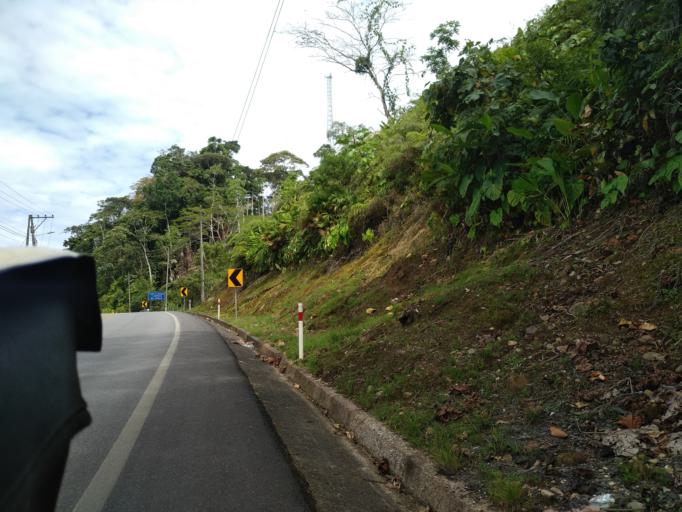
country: EC
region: Napo
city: Tena
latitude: -1.1203
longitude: -77.8164
